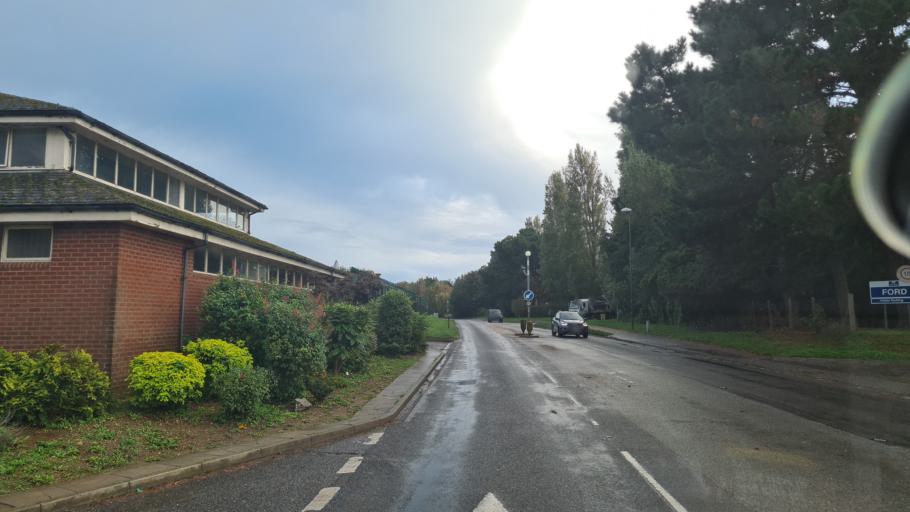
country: GB
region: England
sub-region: West Sussex
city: Littlehampton
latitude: 50.8164
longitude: -0.5800
